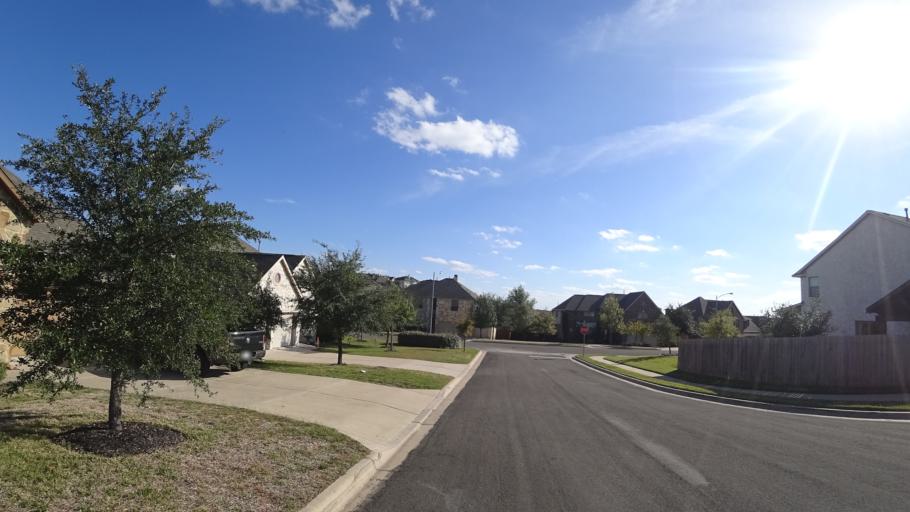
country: US
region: Texas
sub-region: Travis County
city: Barton Creek
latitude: 30.2511
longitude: -97.8794
